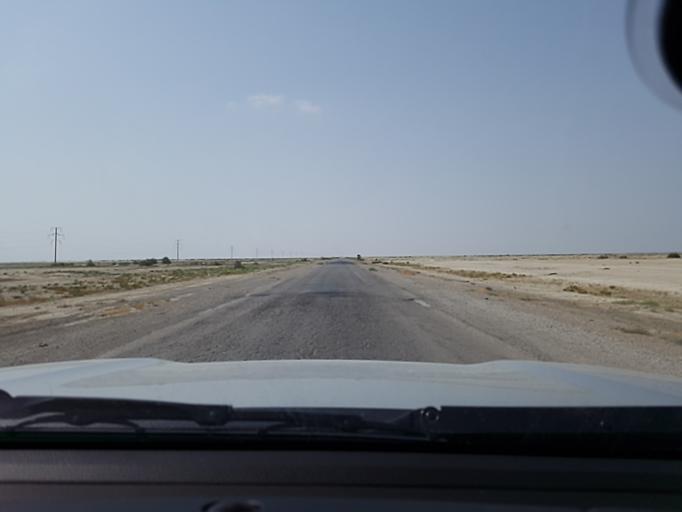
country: TM
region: Balkan
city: Gumdag
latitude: 38.9094
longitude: 54.5918
